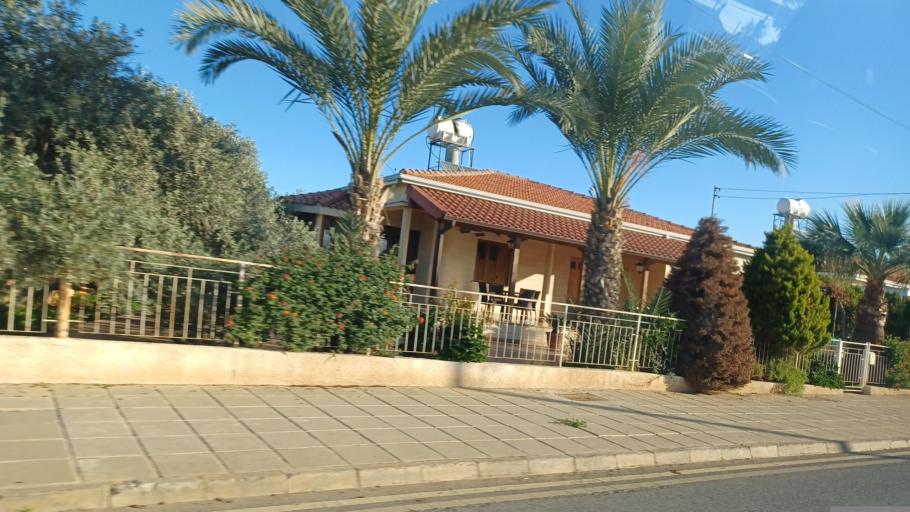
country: CY
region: Lefkosia
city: Astromeritis
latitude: 35.1395
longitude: 33.0480
